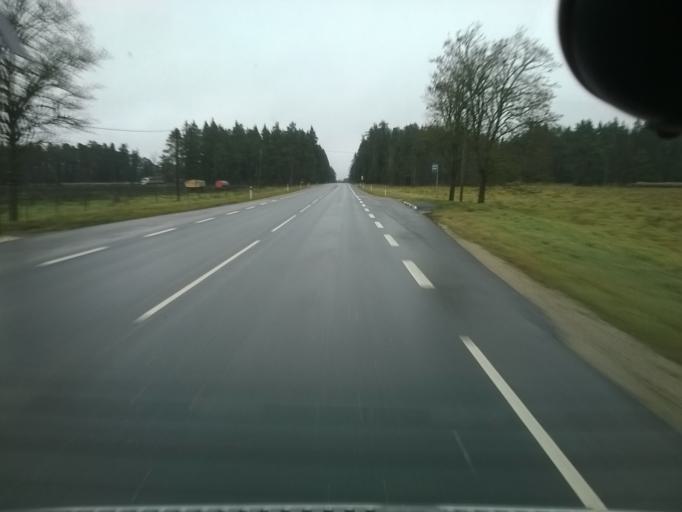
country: EE
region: Harju
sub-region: Nissi vald
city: Turba
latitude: 59.0284
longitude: 24.1527
